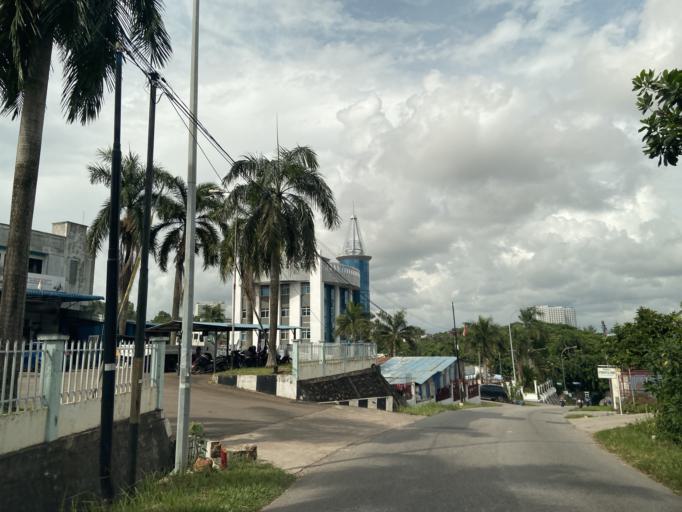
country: SG
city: Singapore
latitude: 1.1508
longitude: 104.0193
